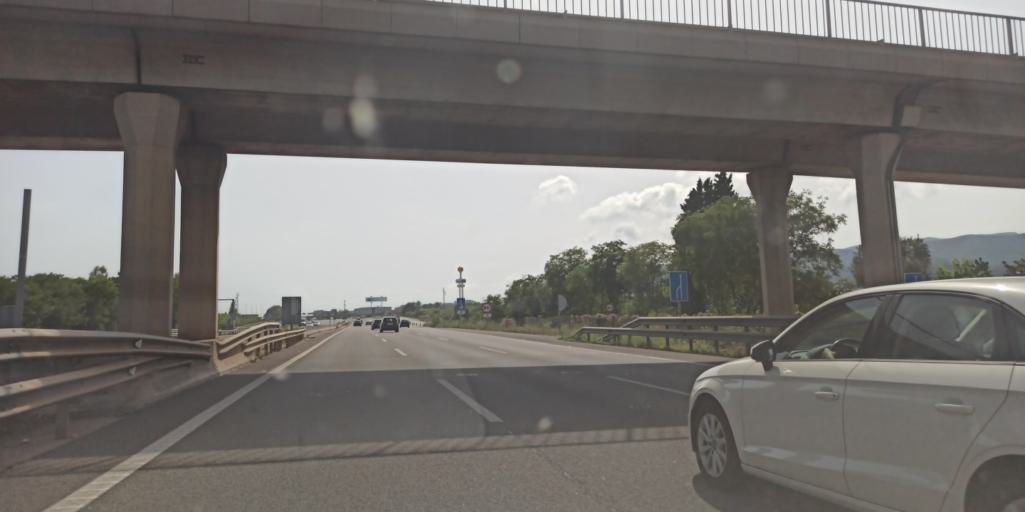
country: ES
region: Catalonia
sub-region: Provincia de Barcelona
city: Gava
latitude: 41.2904
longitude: 2.0067
